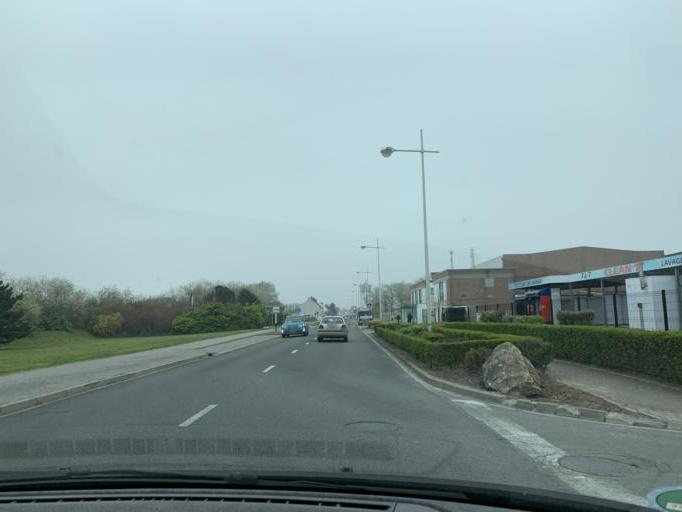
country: FR
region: Nord-Pas-de-Calais
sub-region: Departement du Pas-de-Calais
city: Coquelles
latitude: 50.9567
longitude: 1.8101
